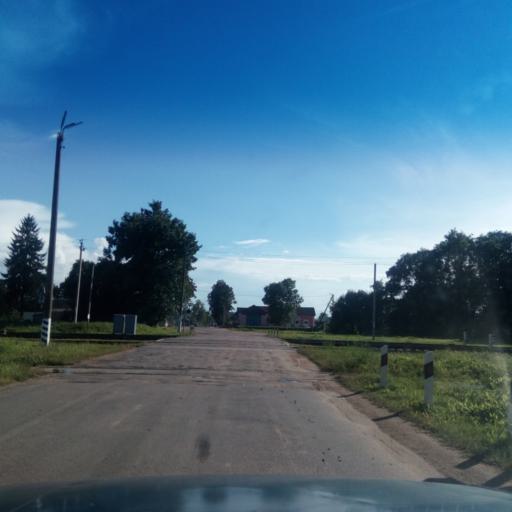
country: BY
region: Vitebsk
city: Dzisna
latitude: 55.6696
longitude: 28.3296
